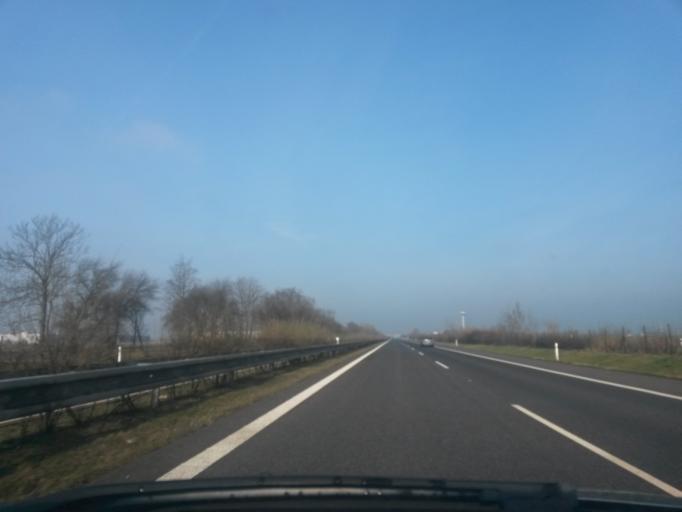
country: CZ
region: Ustecky
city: Zatec
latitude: 50.3775
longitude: 13.5873
